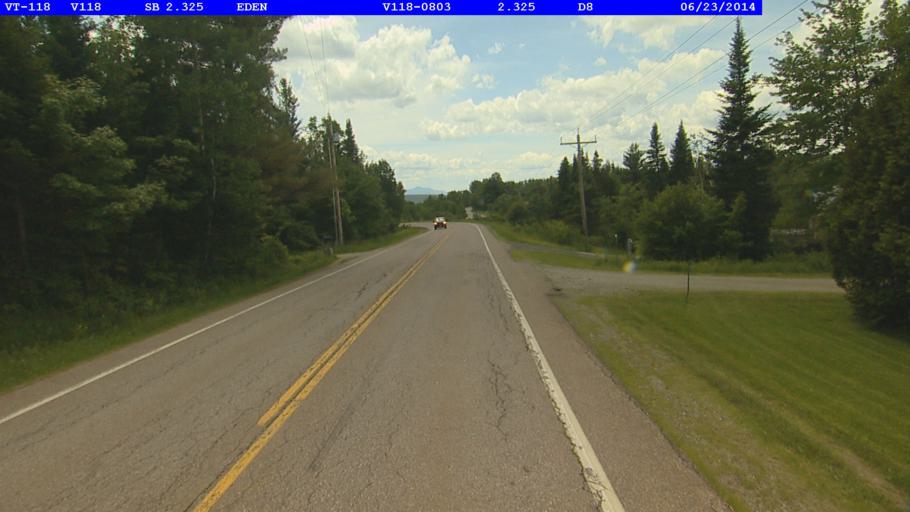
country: US
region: Vermont
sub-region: Lamoille County
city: Hyde Park
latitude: 44.7362
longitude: -72.5672
